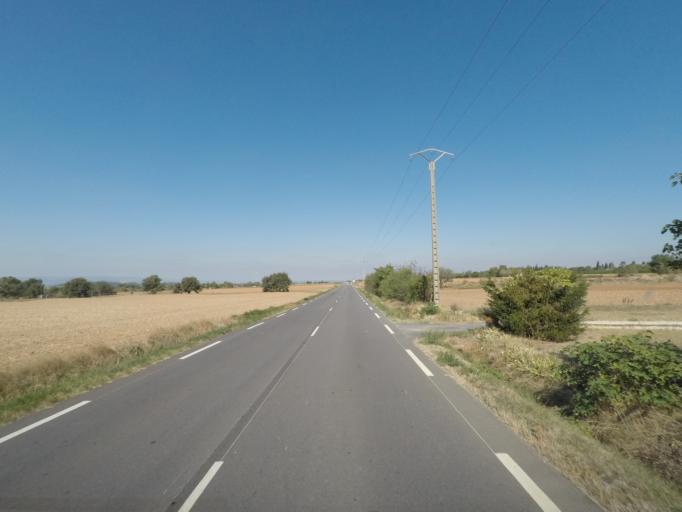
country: FR
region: Rhone-Alpes
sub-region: Departement de la Drome
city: Upie
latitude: 44.8130
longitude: 5.0121
